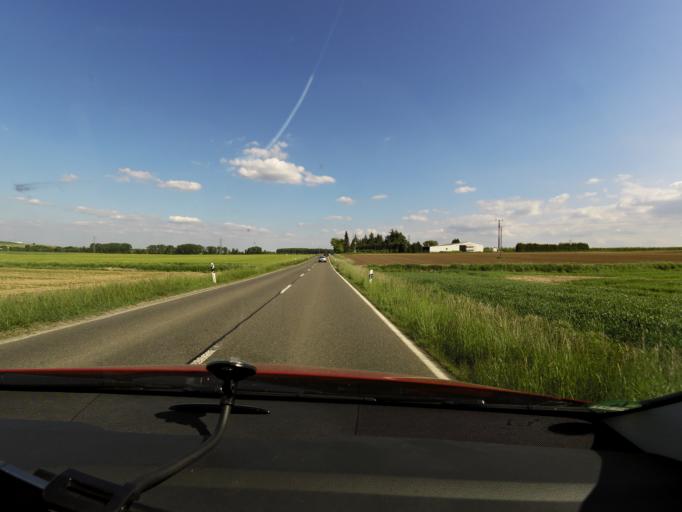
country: DE
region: Rheinland-Pfalz
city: Dernau
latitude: 50.5786
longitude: 7.0492
